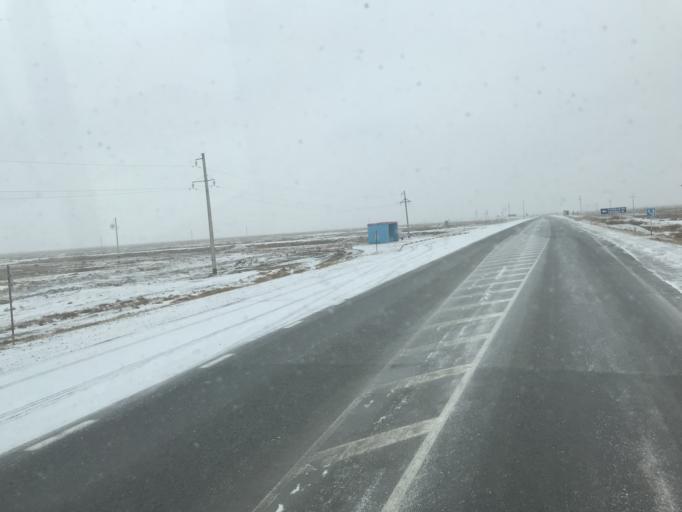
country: KZ
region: Qyzylorda
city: Zhosaly
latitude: 45.4444
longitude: 64.0718
